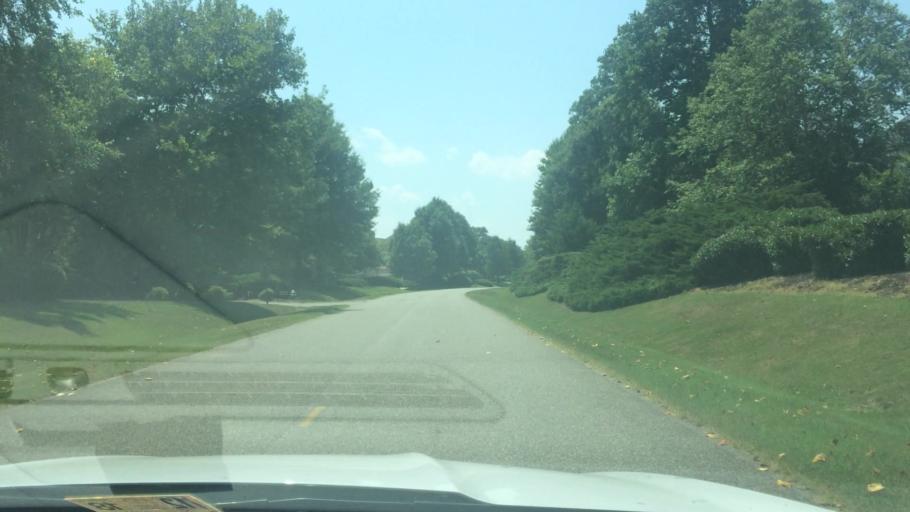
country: US
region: Virginia
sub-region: City of Williamsburg
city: Williamsburg
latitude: 37.2228
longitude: -76.6509
